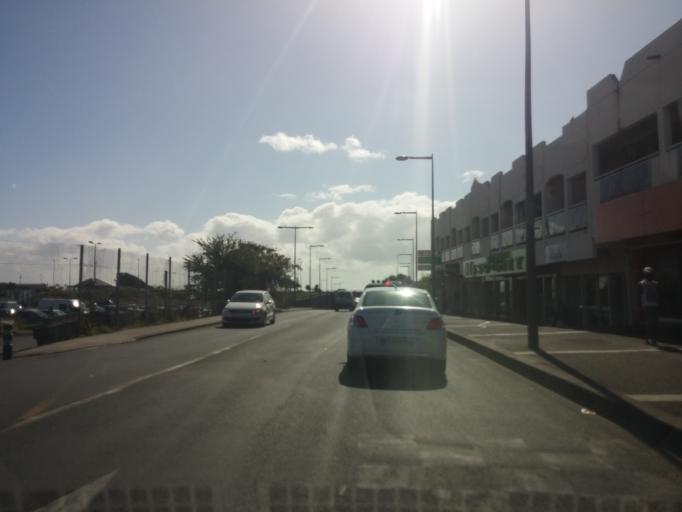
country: RE
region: Reunion
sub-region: Reunion
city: Saint-Denis
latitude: -20.8804
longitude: 55.4575
